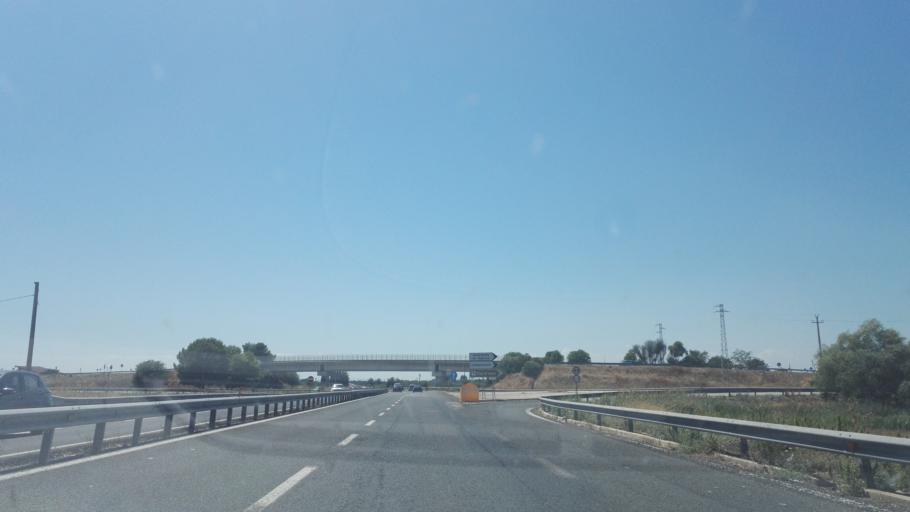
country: IT
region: Apulia
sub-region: Provincia di Taranto
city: Palagiano
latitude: 40.5228
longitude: 17.0285
